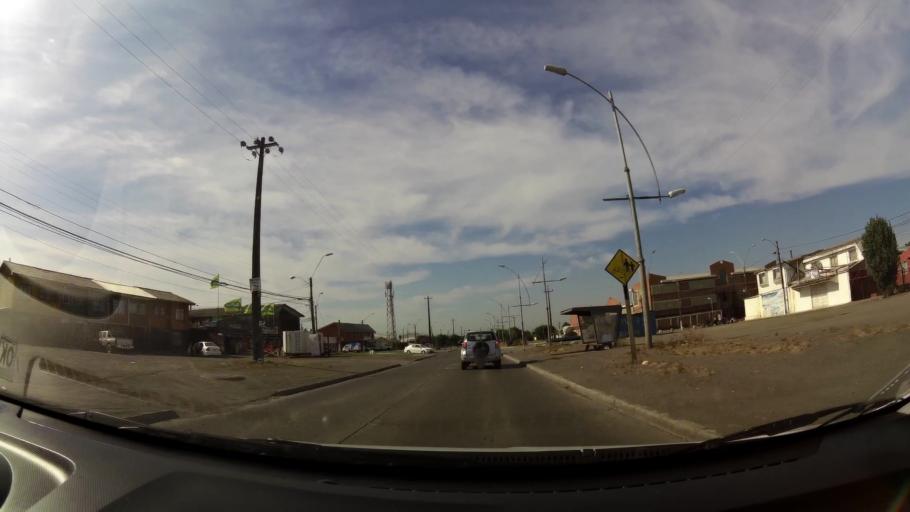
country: CL
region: Biobio
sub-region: Provincia de Concepcion
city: Talcahuano
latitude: -36.7861
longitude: -73.1103
